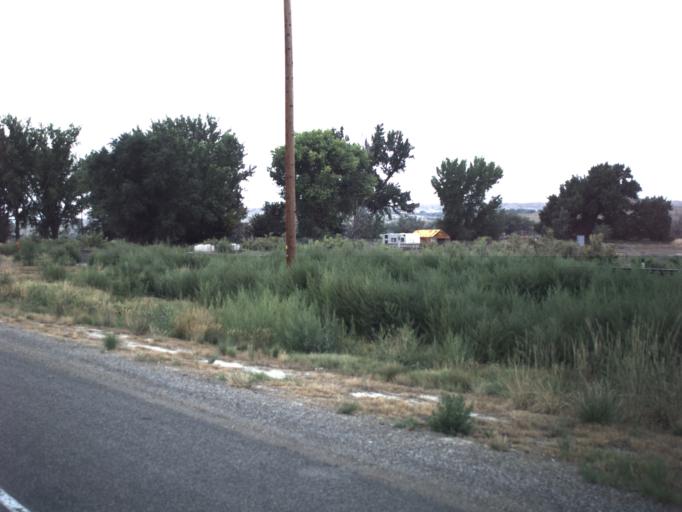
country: US
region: Utah
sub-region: Carbon County
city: Price
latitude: 39.5788
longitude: -110.7861
